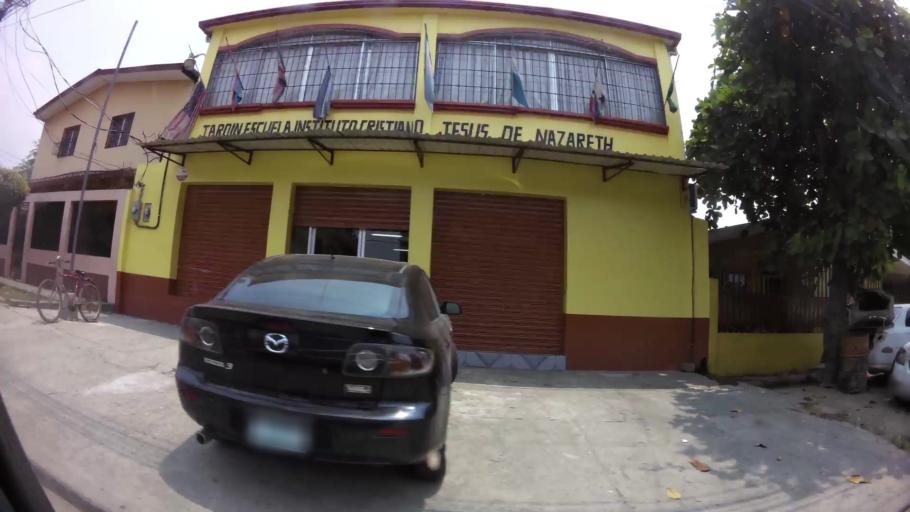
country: HN
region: Cortes
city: San Pedro Sula
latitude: 15.4853
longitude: -88.0109
